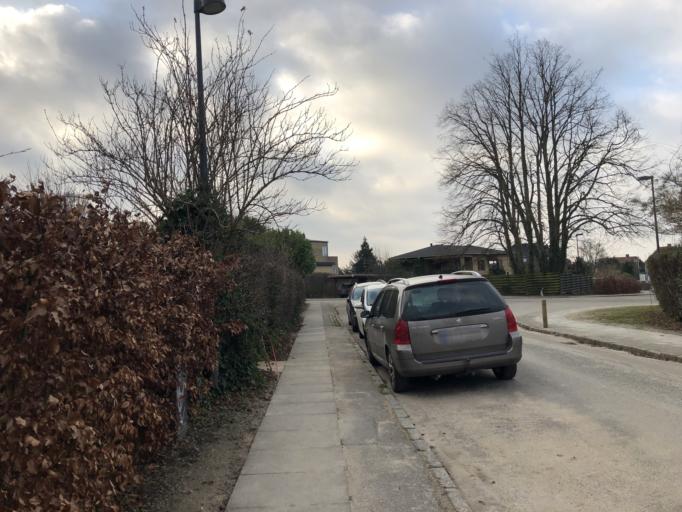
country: DK
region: Capital Region
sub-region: Kobenhavn
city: Vanlose
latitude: 55.7002
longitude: 12.4965
